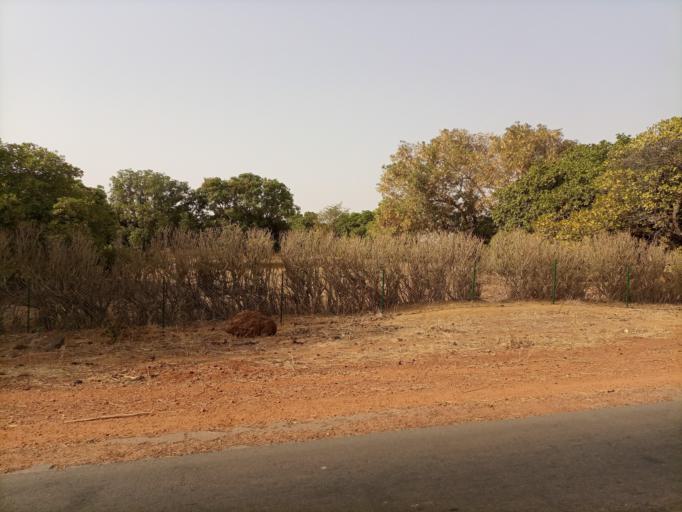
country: SN
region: Fatick
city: Foundiougne
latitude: 14.1221
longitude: -16.4303
